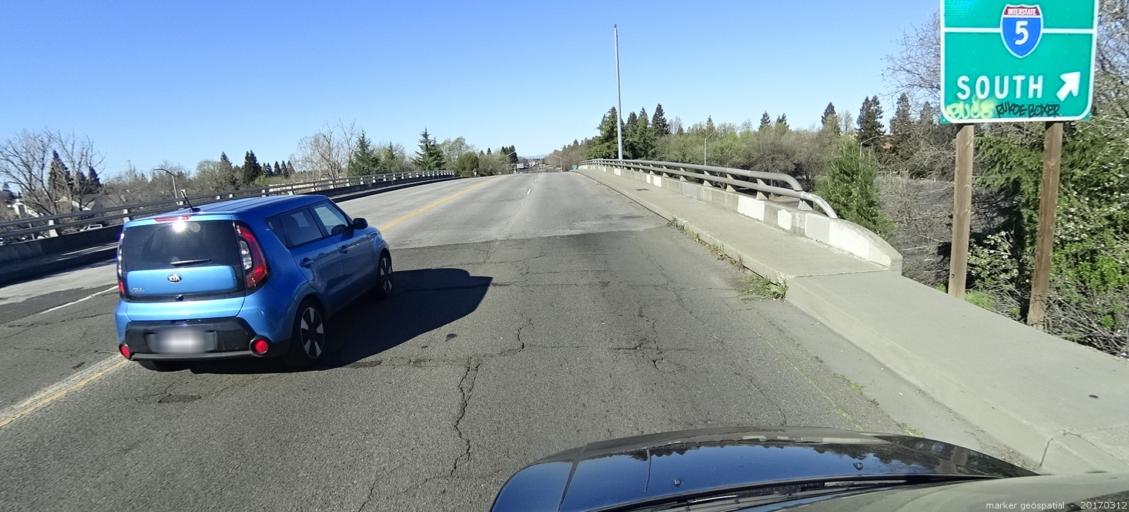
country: US
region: California
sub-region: Sacramento County
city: Sacramento
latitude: 38.6149
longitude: -121.5117
